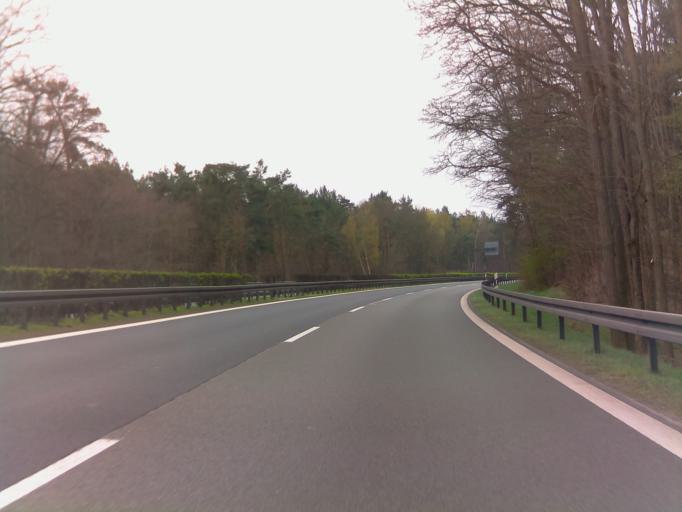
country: DE
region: Brandenburg
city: Werder
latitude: 52.4259
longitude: 12.9294
